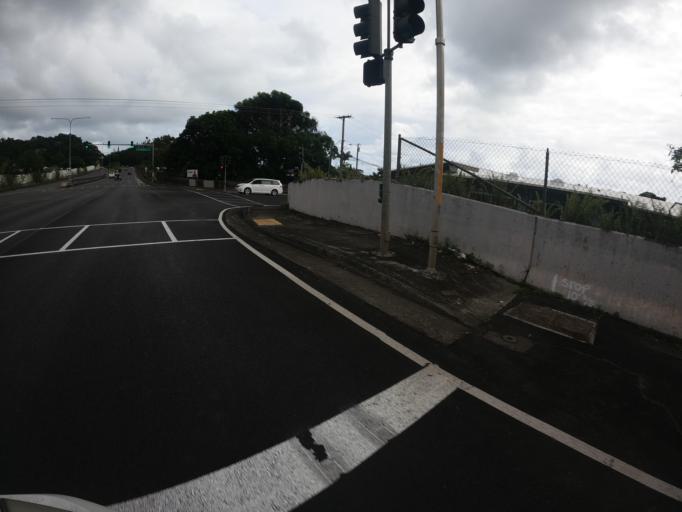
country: US
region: Hawaii
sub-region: Honolulu County
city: Kane'ohe
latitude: 21.4059
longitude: -157.8069
